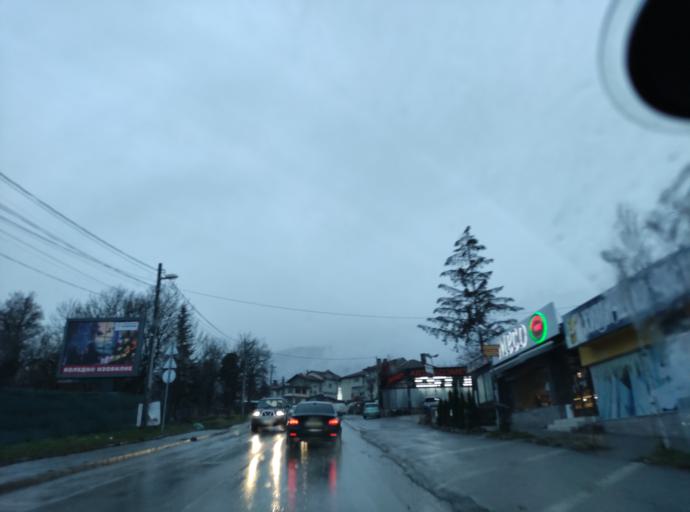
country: BG
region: Sofia-Capital
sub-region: Stolichna Obshtina
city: Sofia
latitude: 42.6355
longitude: 23.3106
